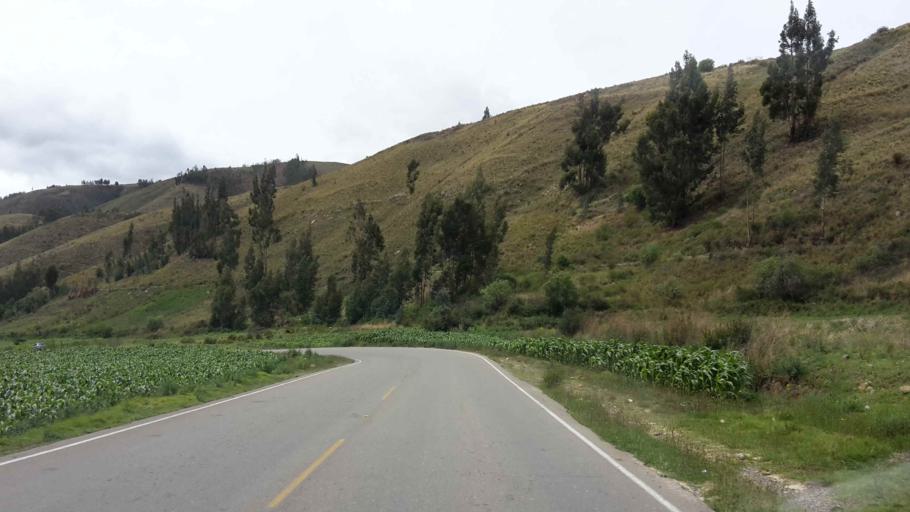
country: BO
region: Cochabamba
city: Colomi
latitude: -17.4115
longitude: -65.7744
